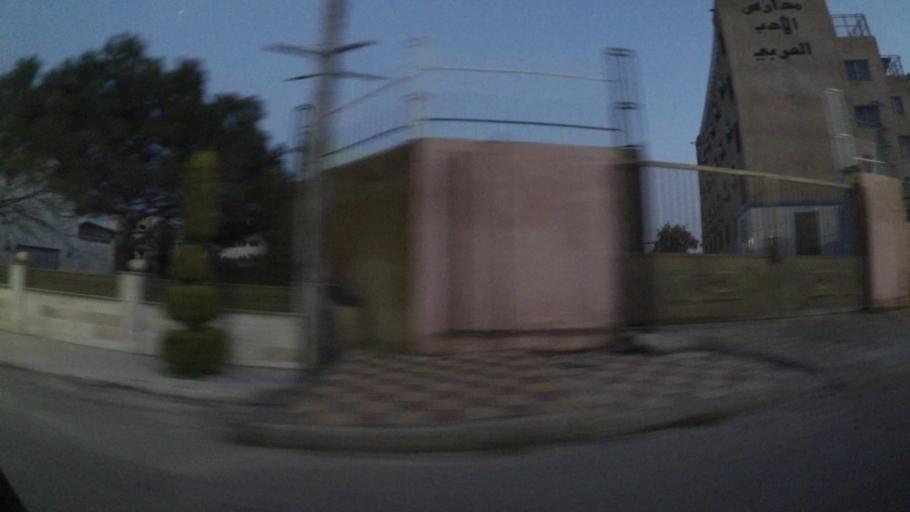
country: JO
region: Amman
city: Al Bunayyat ash Shamaliyah
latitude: 31.8899
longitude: 35.9255
